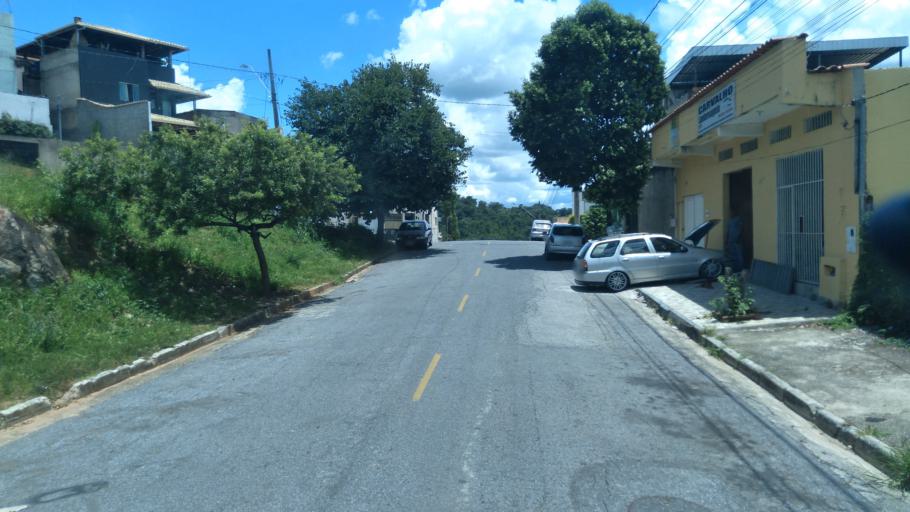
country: BR
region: Minas Gerais
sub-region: Belo Horizonte
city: Belo Horizonte
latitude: -19.8577
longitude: -43.8779
